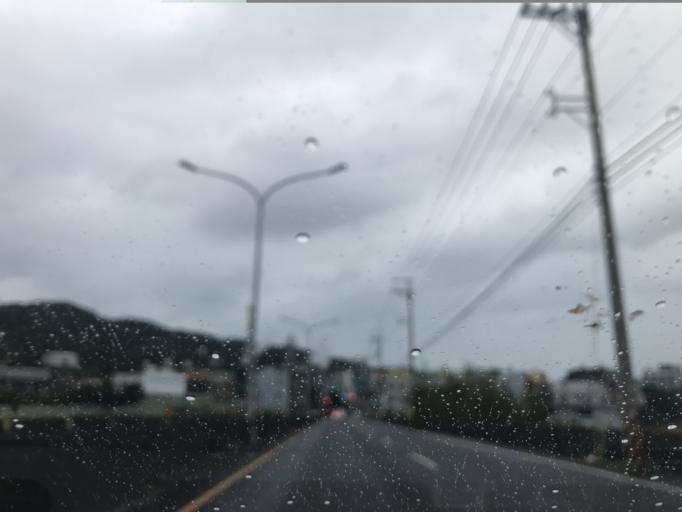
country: TW
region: Taiwan
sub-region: Hsinchu
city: Zhubei
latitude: 24.8251
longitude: 121.0636
